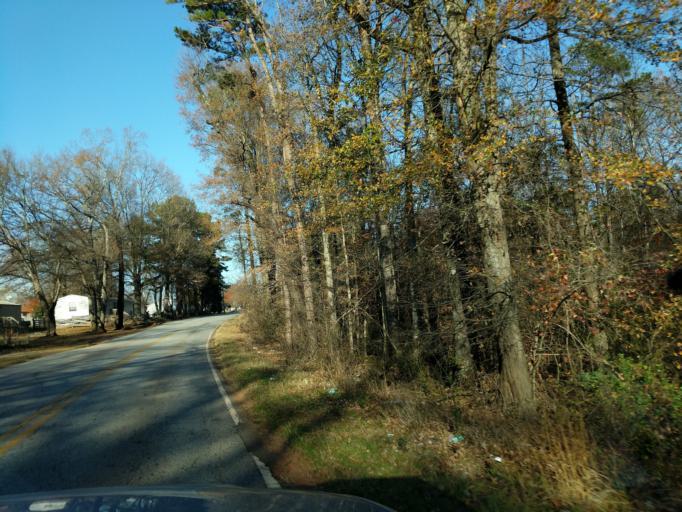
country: US
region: South Carolina
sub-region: Spartanburg County
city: Wellford
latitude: 34.9192
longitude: -82.0816
